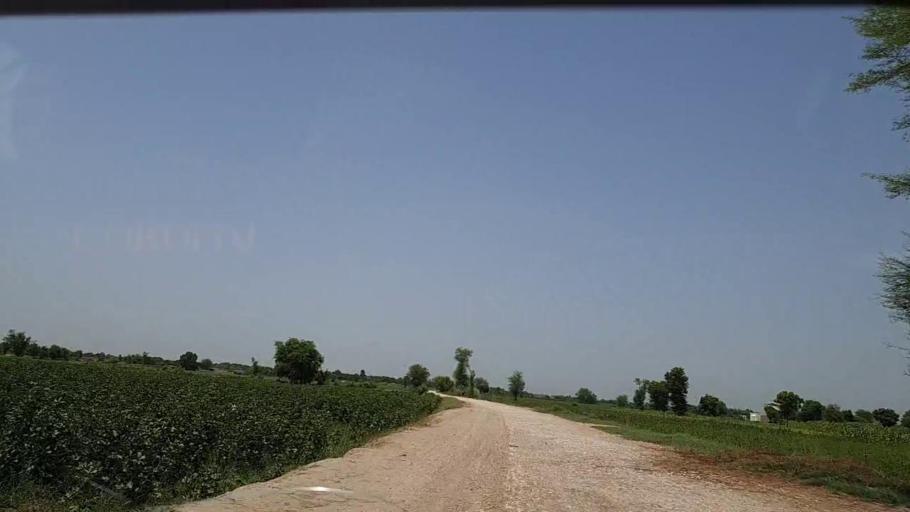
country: PK
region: Sindh
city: Tharu Shah
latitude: 26.9556
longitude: 68.0433
